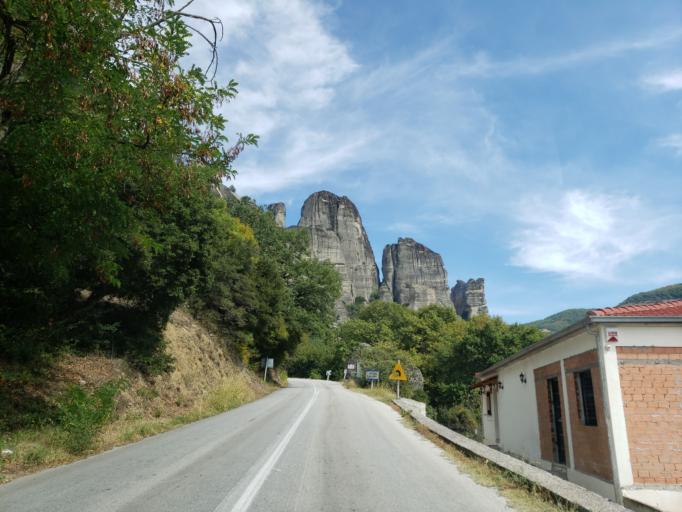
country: GR
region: Thessaly
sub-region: Trikala
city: Kastraki
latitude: 39.7215
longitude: 21.6215
